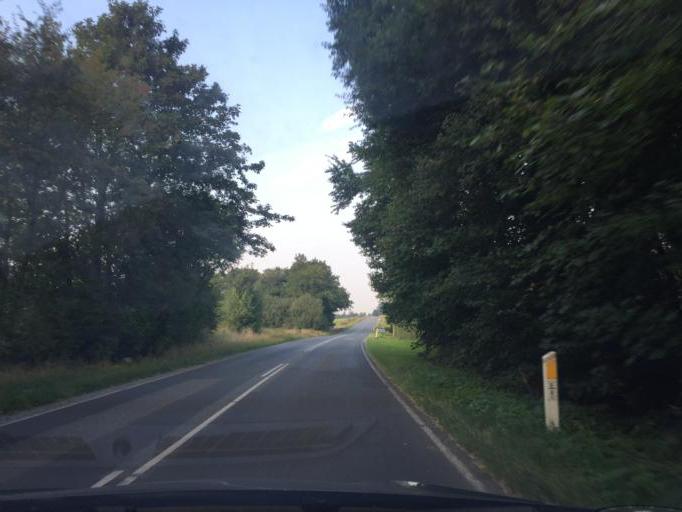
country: DK
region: South Denmark
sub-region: Kerteminde Kommune
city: Langeskov
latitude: 55.2987
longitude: 10.5727
